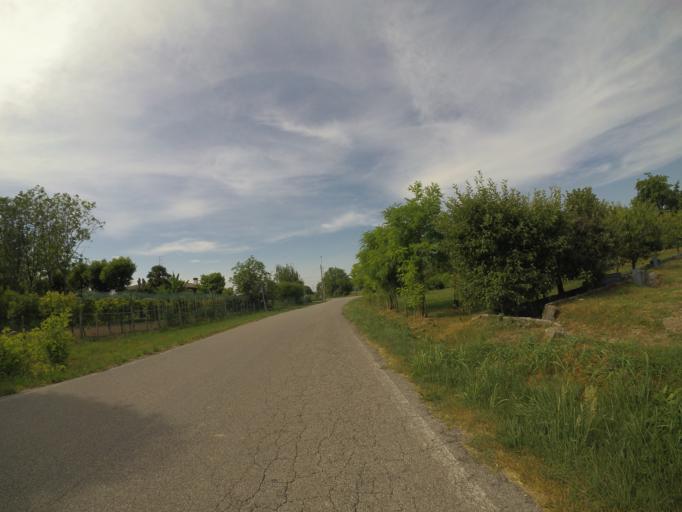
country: IT
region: Friuli Venezia Giulia
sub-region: Provincia di Udine
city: Camino al Tagliamento
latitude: 45.9487
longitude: 12.9396
